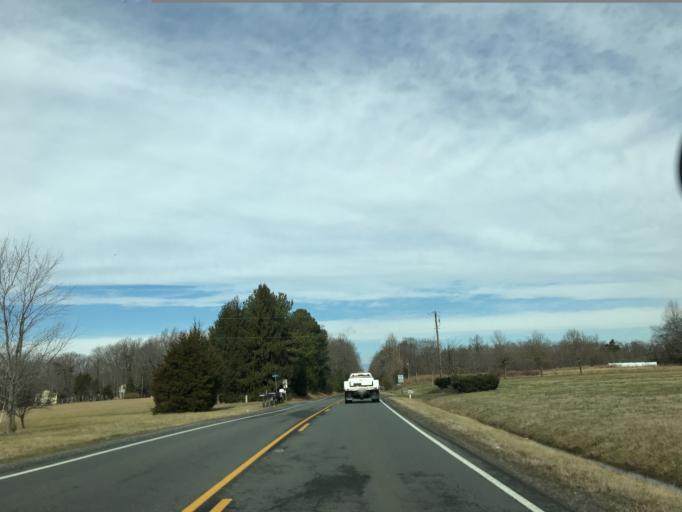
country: US
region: Virginia
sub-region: King George County
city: Dahlgren
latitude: 38.3007
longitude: -77.0733
